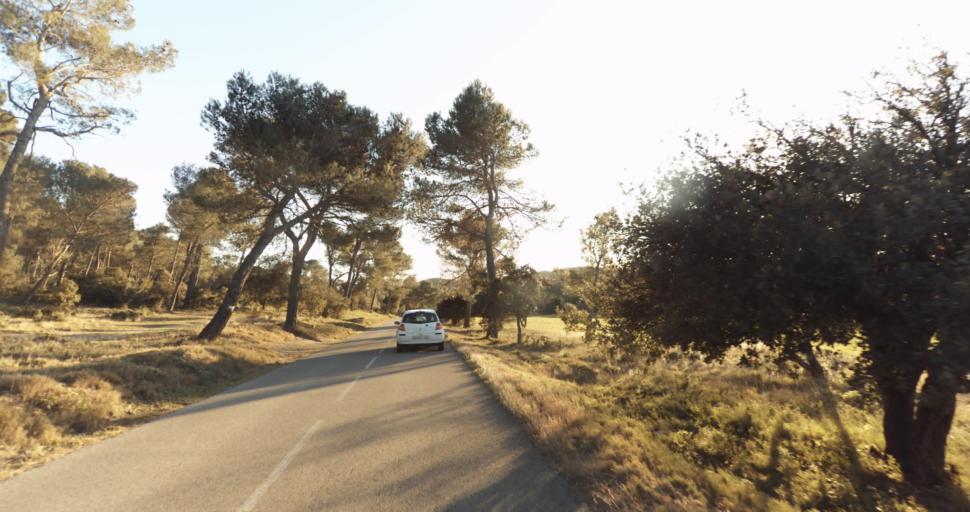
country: FR
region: Provence-Alpes-Cote d'Azur
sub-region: Departement des Bouches-du-Rhone
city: Barbentane
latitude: 43.8695
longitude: 4.7297
